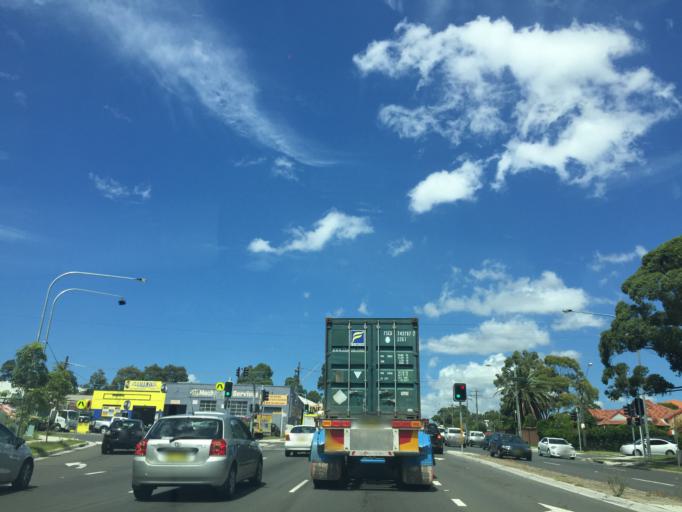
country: AU
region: New South Wales
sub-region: Strathfield
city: Strathfield South
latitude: -33.8948
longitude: 151.0663
